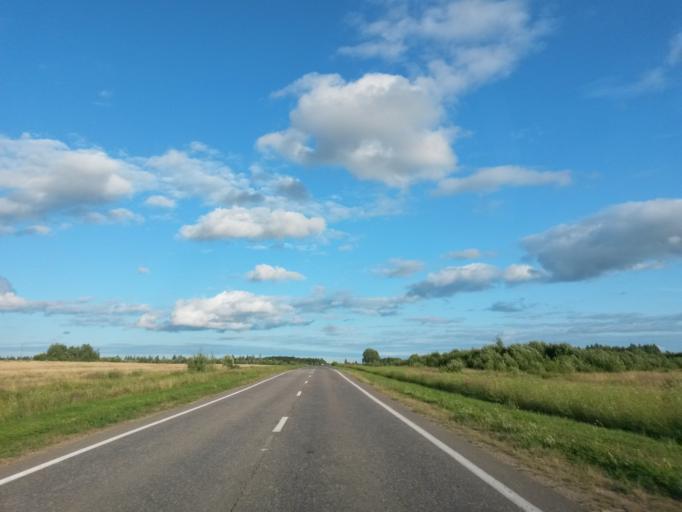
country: RU
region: Jaroslavl
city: Konstantinovskiy
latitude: 57.8740
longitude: 39.5889
